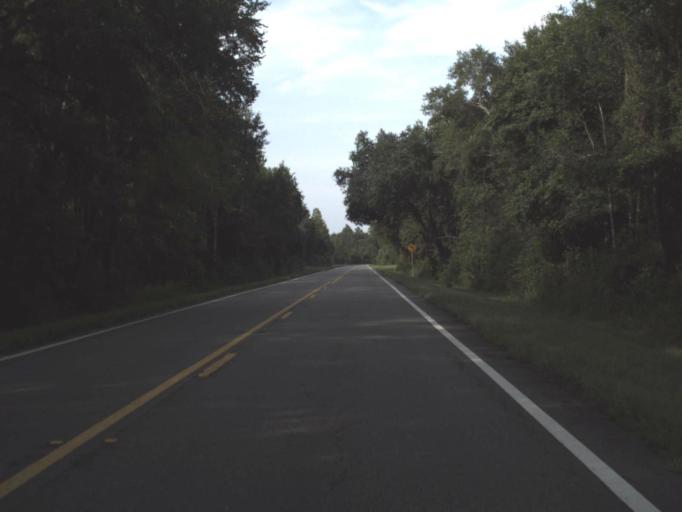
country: US
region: Florida
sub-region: Madison County
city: Madison
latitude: 30.3940
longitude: -83.6556
